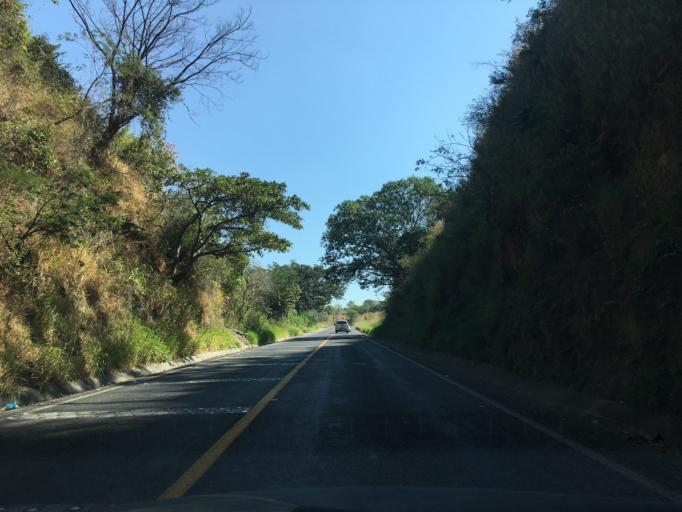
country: MX
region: Michoacan
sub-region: Gabriel Zamora
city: Lombardia
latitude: 19.2234
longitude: -102.0481
